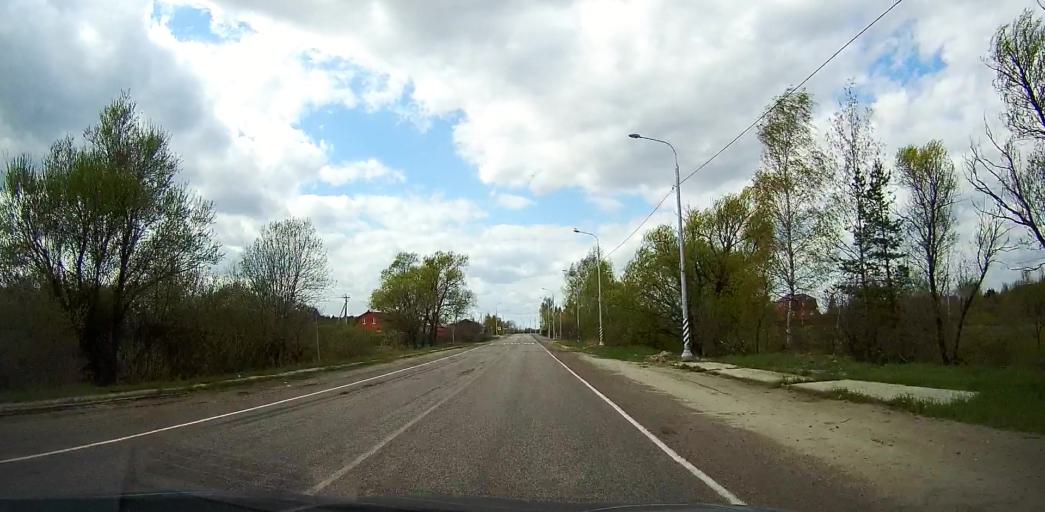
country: RU
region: Moskovskaya
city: Davydovo
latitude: 55.6642
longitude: 38.8026
